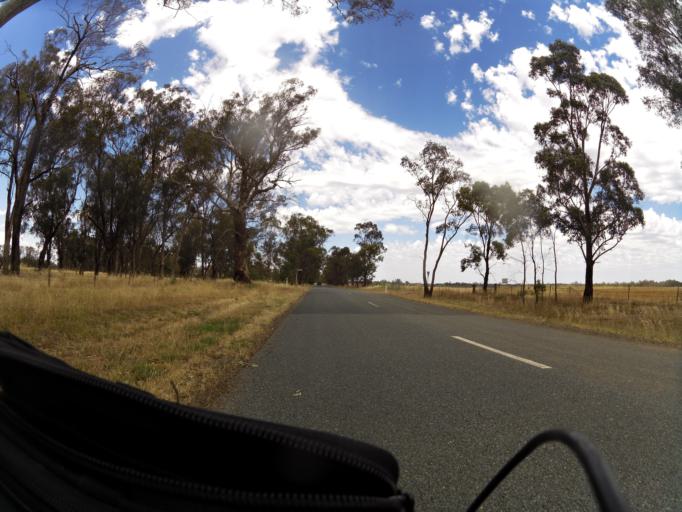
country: AU
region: Victoria
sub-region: Greater Shepparton
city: Shepparton
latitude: -36.6601
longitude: 145.1998
